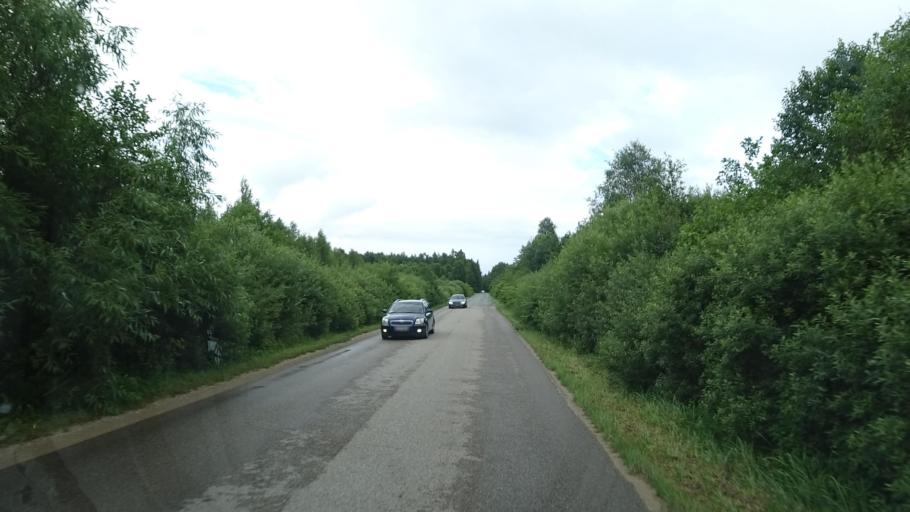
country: LV
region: Liepaja
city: Vec-Liepaja
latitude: 56.5998
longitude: 21.0310
